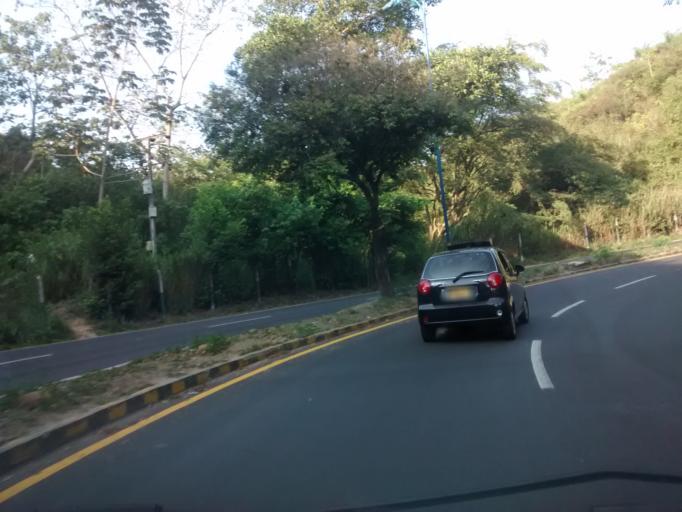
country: CO
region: Santander
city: Bucaramanga
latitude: 7.0913
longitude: -73.1320
